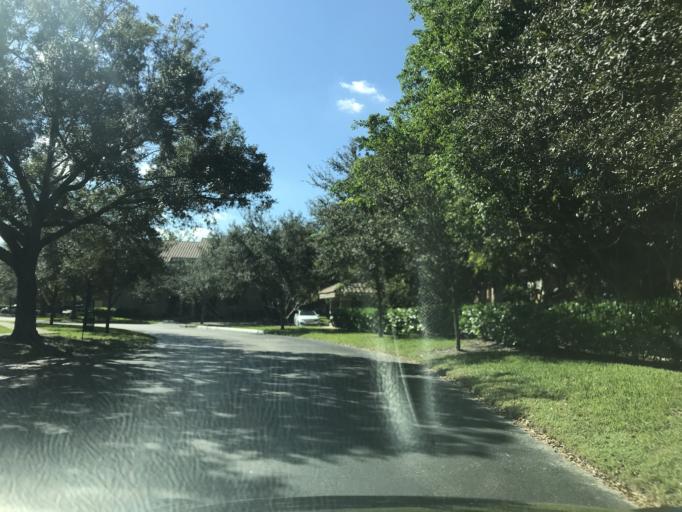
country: US
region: Florida
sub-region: Broward County
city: Pine Island Ridge
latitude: 26.1324
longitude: -80.2698
